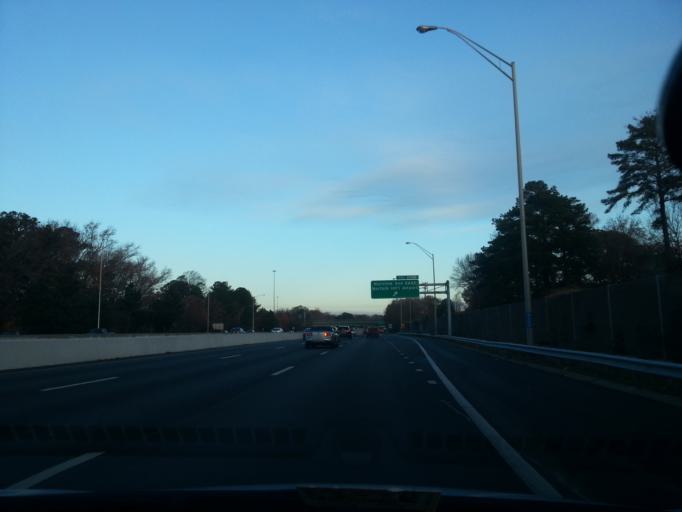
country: US
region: Virginia
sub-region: City of Norfolk
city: Norfolk
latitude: 36.8881
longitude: -76.2286
